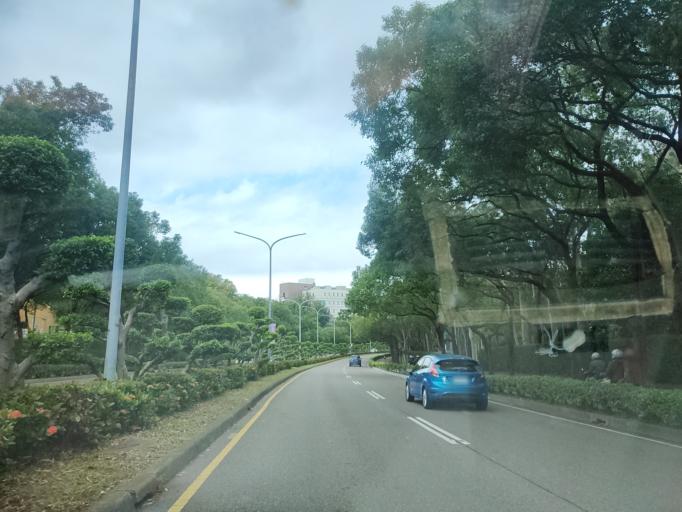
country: TW
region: Taiwan
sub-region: Hsinchu
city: Hsinchu
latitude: 24.7778
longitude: 121.0078
